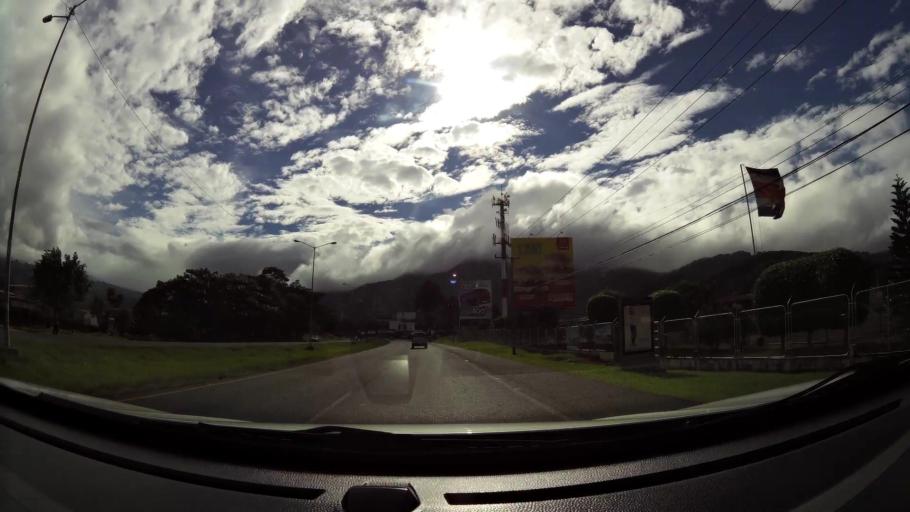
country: CR
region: Cartago
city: San Diego
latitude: 9.9019
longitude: -84.0068
